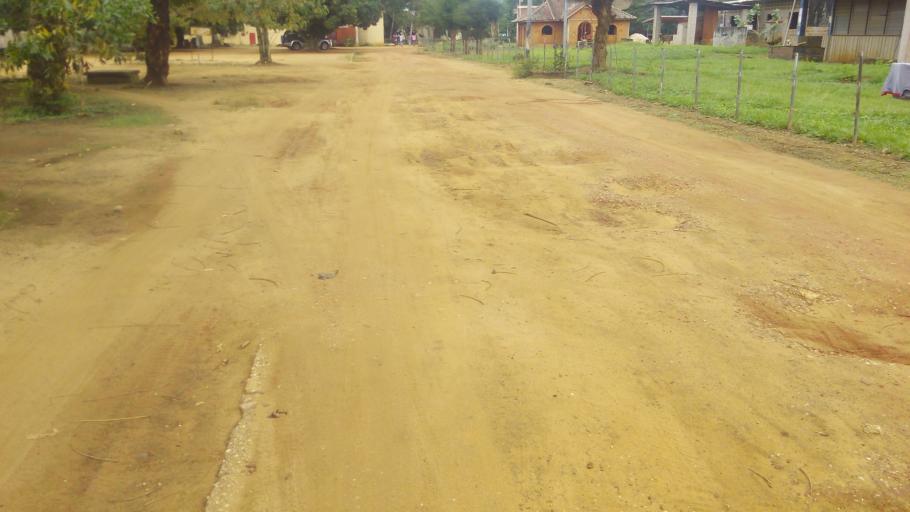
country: BJ
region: Atlantique
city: Abomey-Calavi
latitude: 6.4154
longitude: 2.3417
